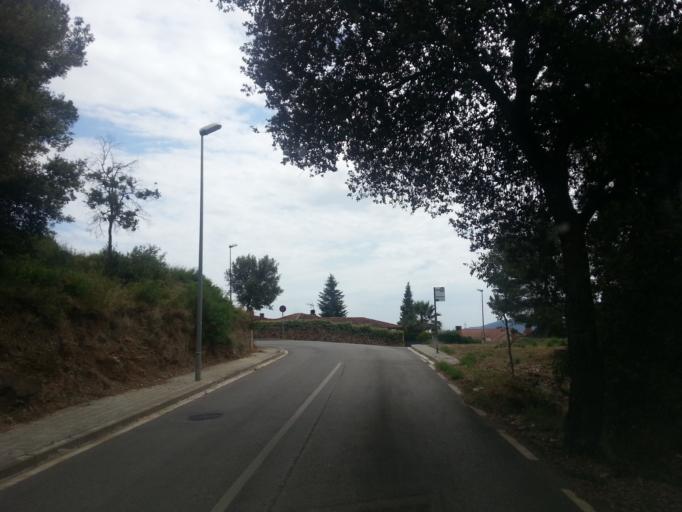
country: ES
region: Catalonia
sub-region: Provincia de Barcelona
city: Molins de Rei
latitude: 41.4291
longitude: 2.0385
